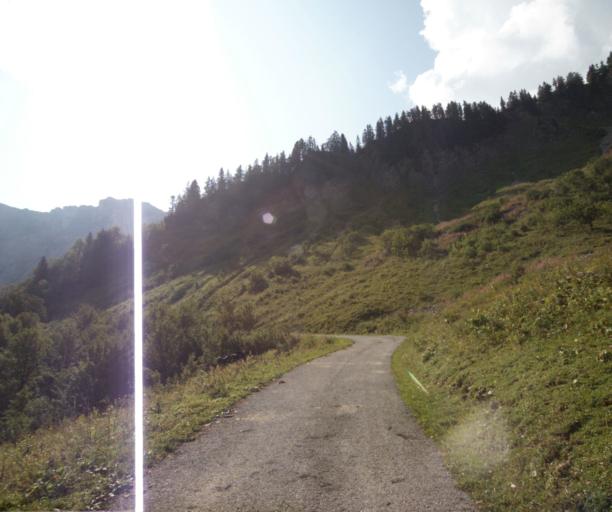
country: CH
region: Vaud
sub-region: Riviera-Pays-d'Enhaut District
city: Caux
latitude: 46.4261
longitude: 6.9983
